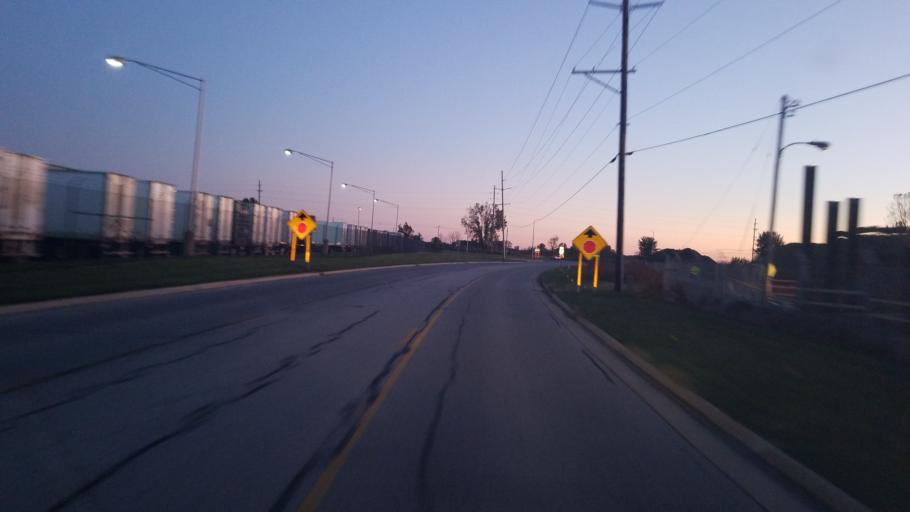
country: US
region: Ohio
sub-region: Marion County
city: Marion
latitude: 40.5882
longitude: -83.1768
